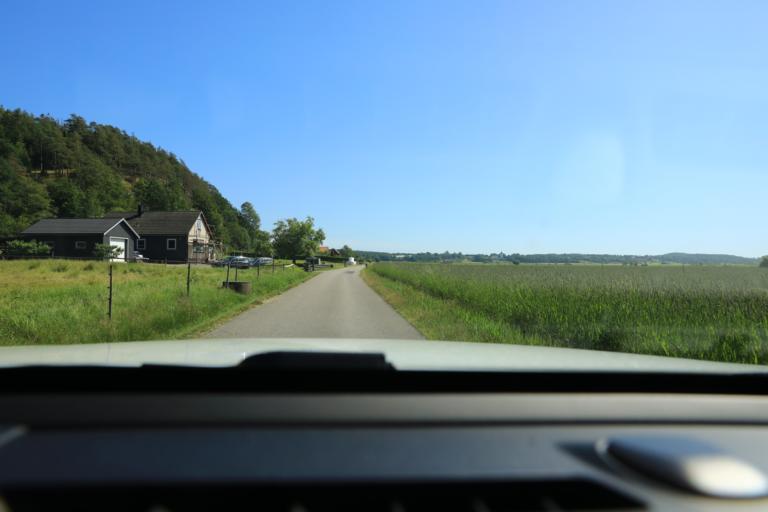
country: SE
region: Halland
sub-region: Varbergs Kommun
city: Veddige
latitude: 57.1757
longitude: 12.3156
